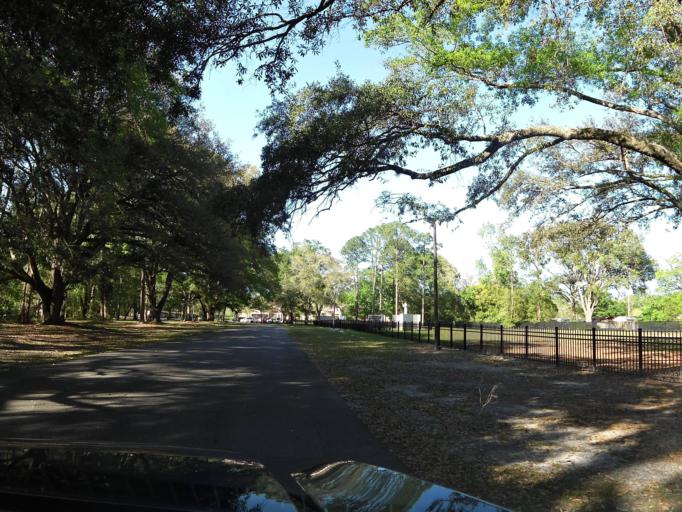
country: US
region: Florida
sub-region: Duval County
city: Jacksonville
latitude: 30.2779
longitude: -81.5982
